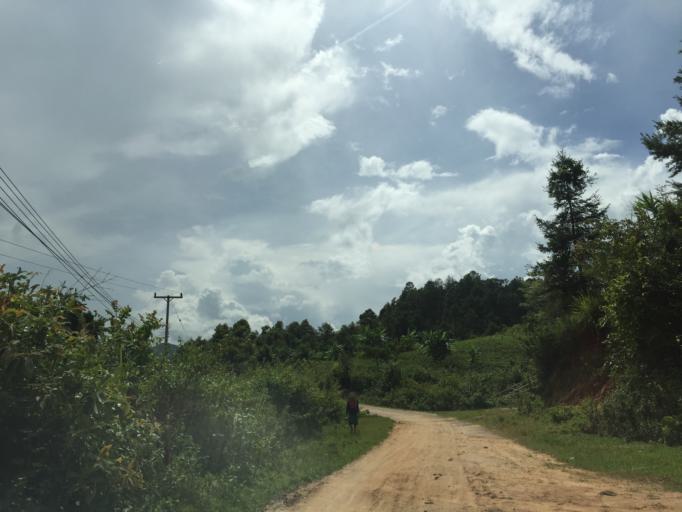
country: LA
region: Xiangkhoang
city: Muang Phonsavan
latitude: 19.3412
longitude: 103.5408
